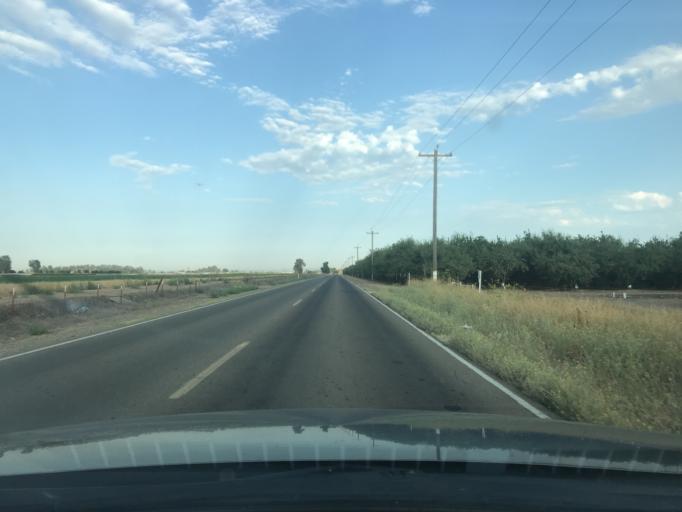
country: US
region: California
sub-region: Merced County
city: Merced
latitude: 37.3608
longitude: -120.5325
